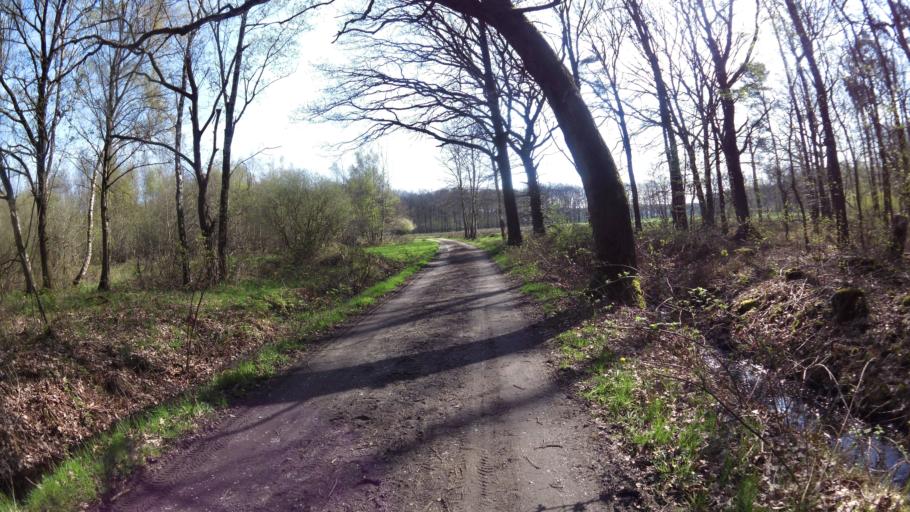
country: DE
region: North Rhine-Westphalia
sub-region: Regierungsbezirk Koln
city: Gangelt
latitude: 50.9814
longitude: 6.0124
